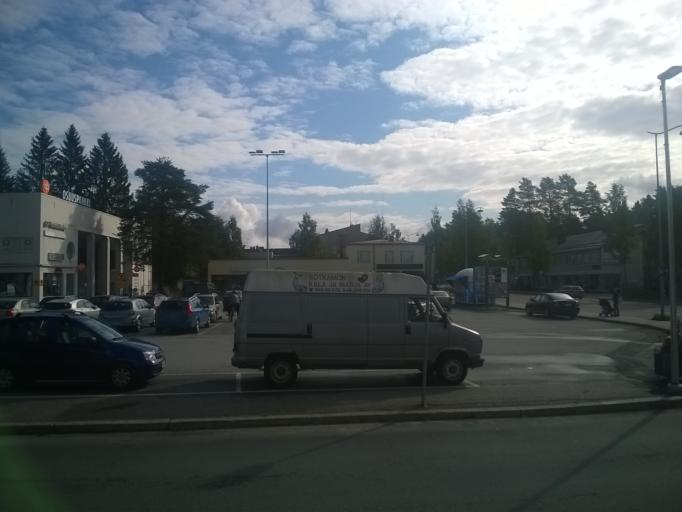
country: FI
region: Kainuu
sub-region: Kajaani
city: Sotkamo
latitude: 64.1309
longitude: 28.3842
